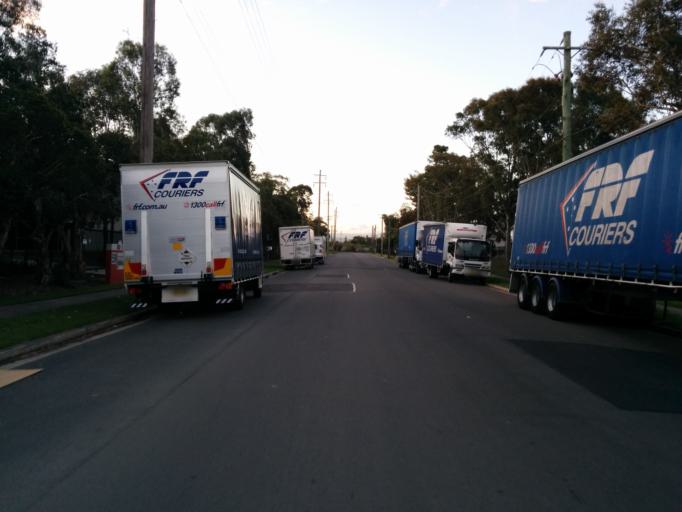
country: AU
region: New South Wales
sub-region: Fairfield
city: Fairfield East
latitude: -33.8627
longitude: 150.9631
